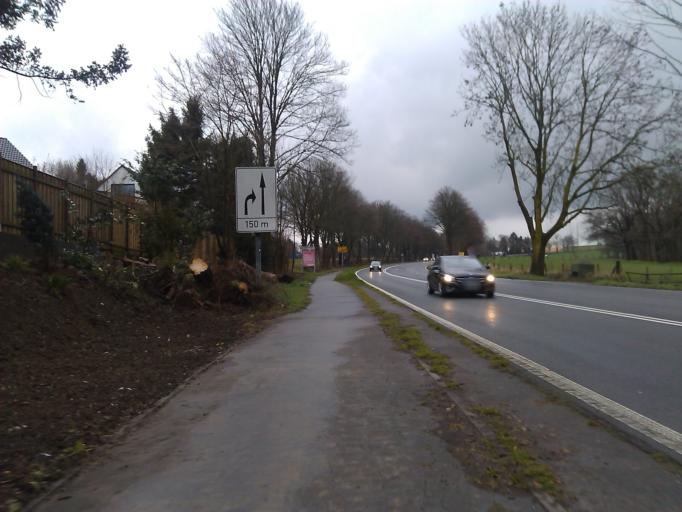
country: DE
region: North Rhine-Westphalia
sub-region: Regierungsbezirk Dusseldorf
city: Heiligenhaus
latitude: 51.3746
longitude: 6.9321
